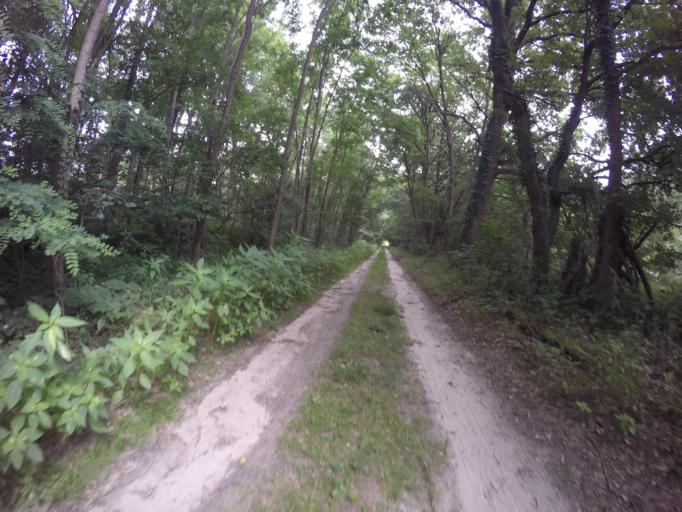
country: DE
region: Lower Saxony
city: Thomasburg
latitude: 53.2582
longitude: 10.6958
